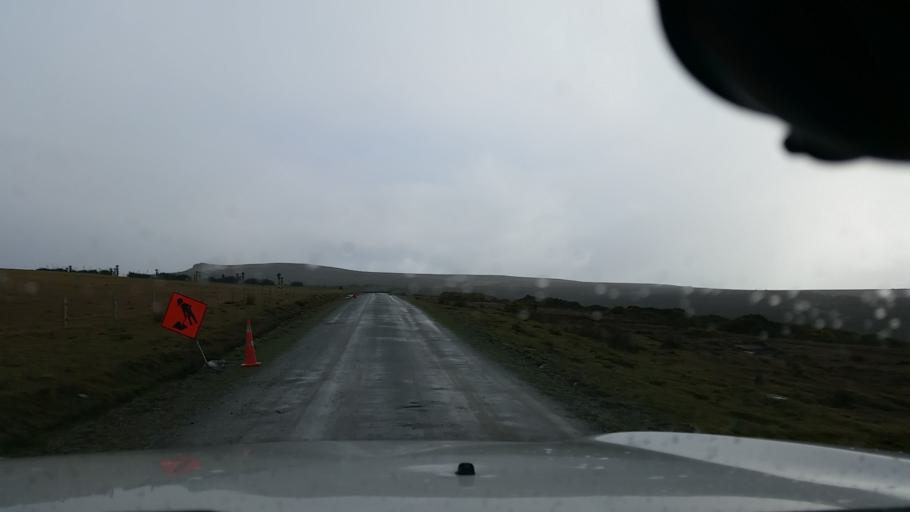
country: NZ
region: Chatham Islands
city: Waitangi
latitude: -43.8047
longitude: -176.7165
